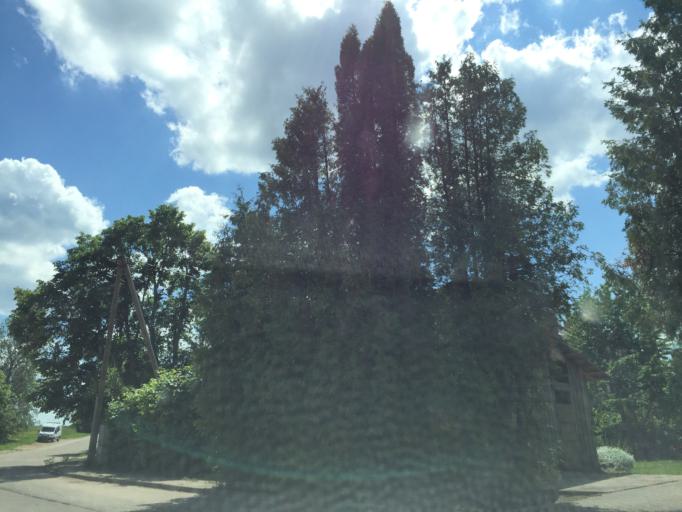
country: LV
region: Priekuli
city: Priekuli
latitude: 57.2615
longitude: 25.4269
